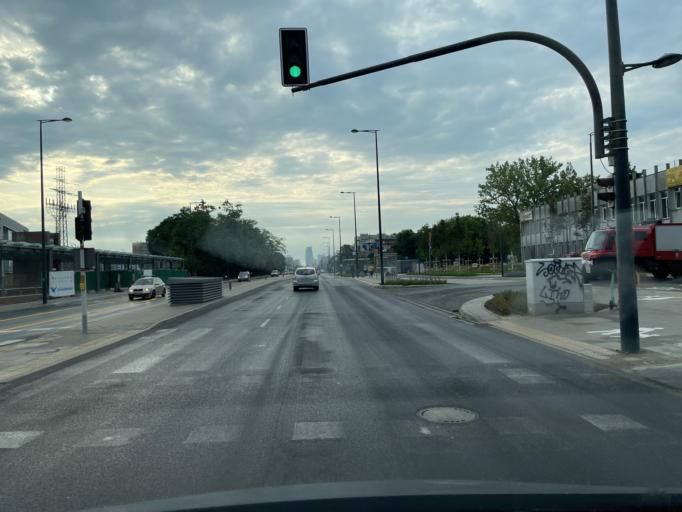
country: PL
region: Masovian Voivodeship
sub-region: Warszawa
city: Bemowo
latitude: 52.2405
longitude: 20.9293
